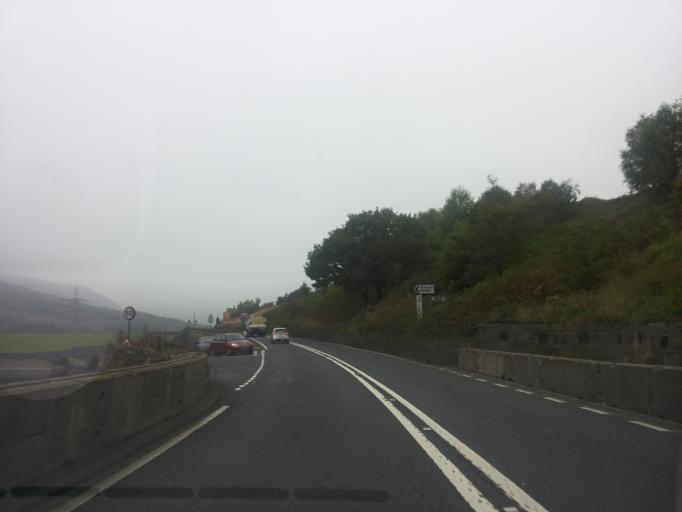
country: GB
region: England
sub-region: Derbyshire
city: Glossop
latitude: 53.4938
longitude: -1.8775
